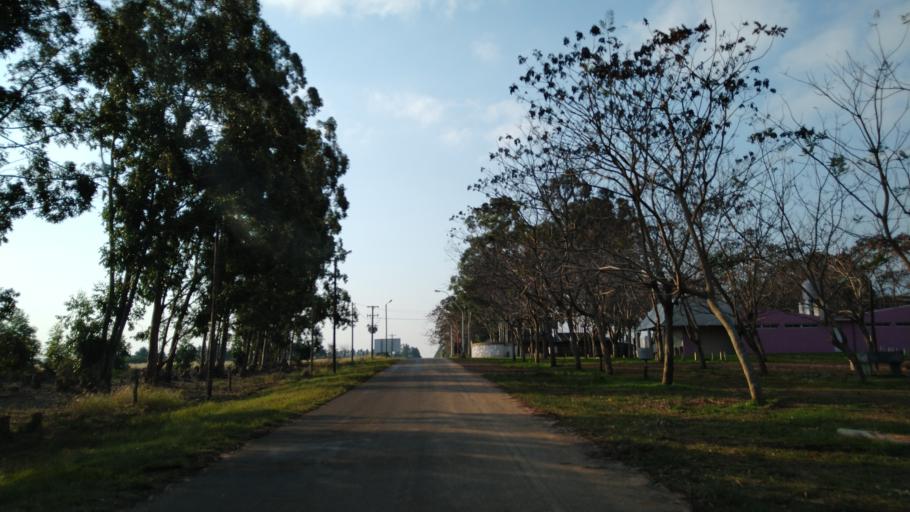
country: AR
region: Entre Rios
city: Santa Ana
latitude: -30.9135
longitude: -57.9269
